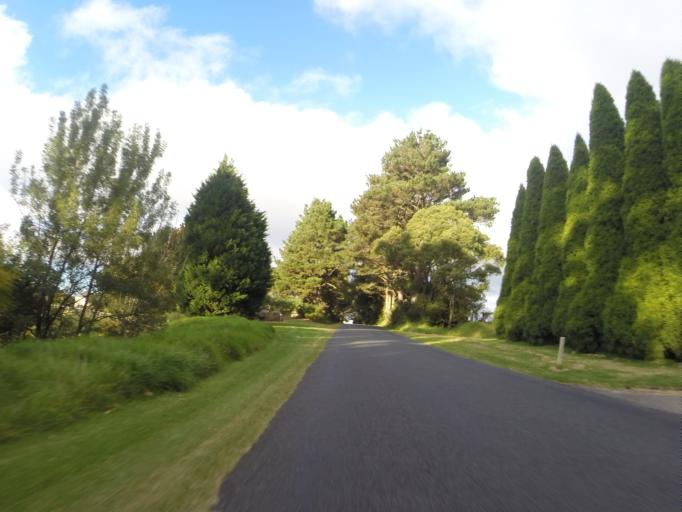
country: AU
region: New South Wales
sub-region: Shoalhaven Shire
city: Kangaroo Valley
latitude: -34.6012
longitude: 150.5534
